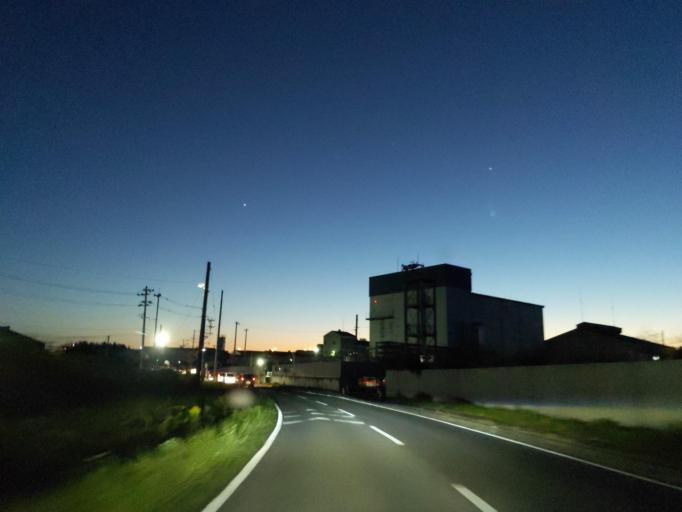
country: JP
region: Fukushima
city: Sukagawa
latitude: 37.3056
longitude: 140.3783
